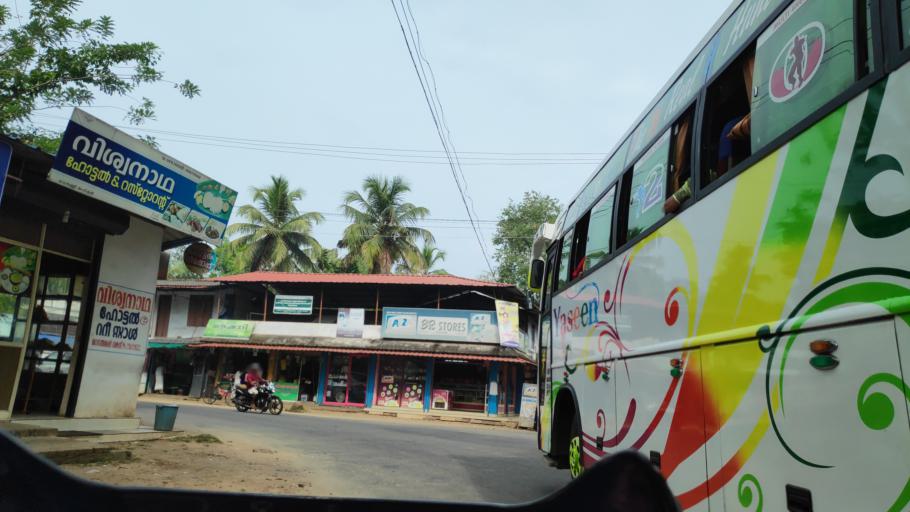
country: IN
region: Kerala
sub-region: Alappuzha
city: Kutiatodu
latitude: 9.8208
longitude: 76.3502
